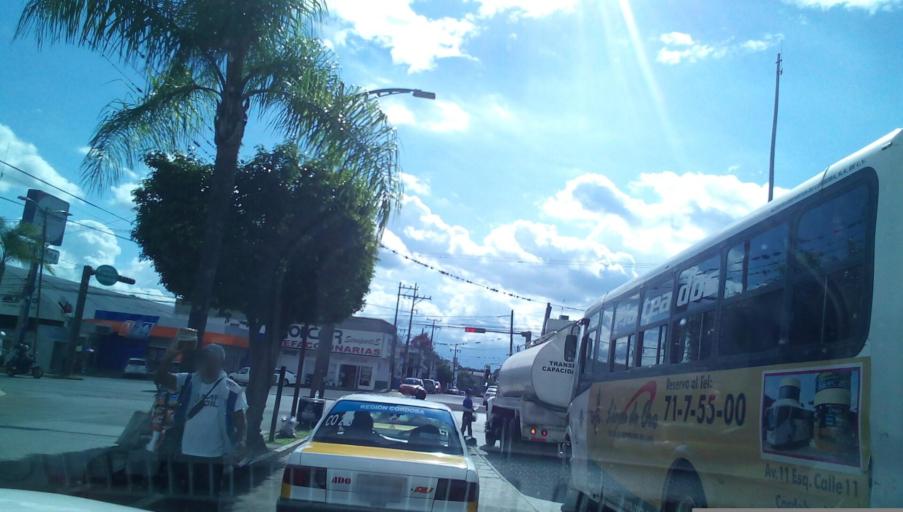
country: MX
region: Veracruz
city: Cordoba
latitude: 18.8808
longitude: -96.9210
